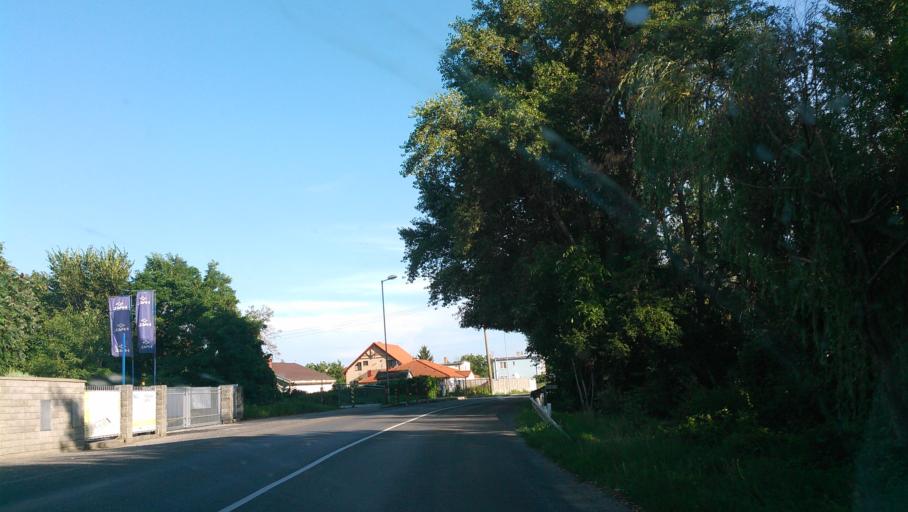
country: SK
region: Bratislavsky
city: Svaty Jur
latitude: 48.1916
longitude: 17.2491
